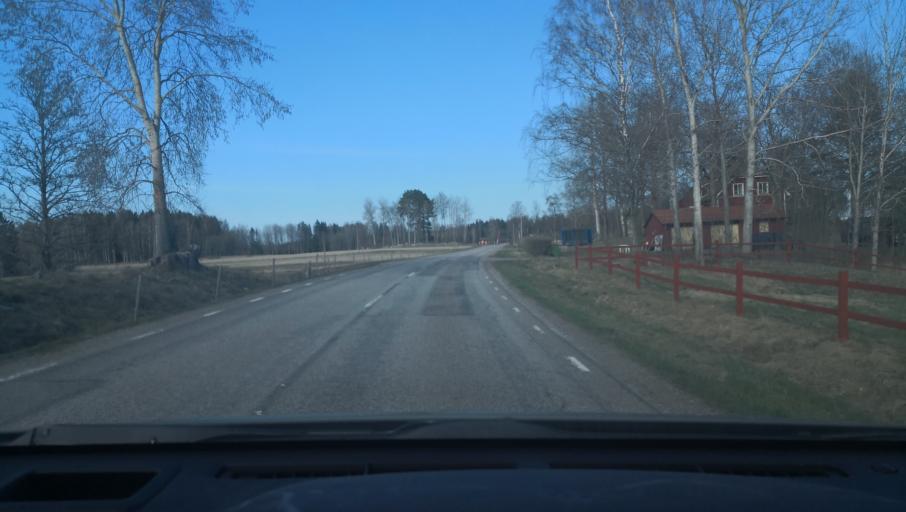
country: SE
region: Uppsala
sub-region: Heby Kommun
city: Heby
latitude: 59.9603
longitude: 16.8858
